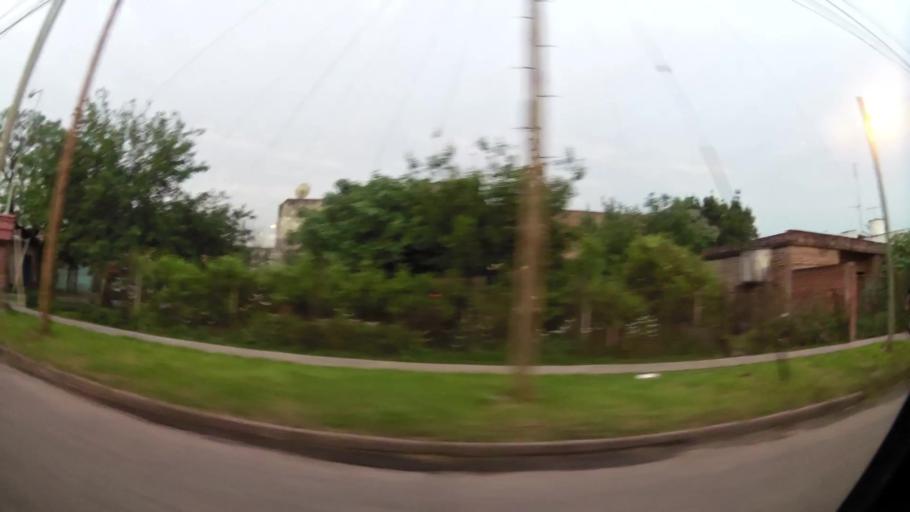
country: AR
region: Buenos Aires
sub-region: Partido de Lomas de Zamora
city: Lomas de Zamora
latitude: -34.7428
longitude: -58.3715
